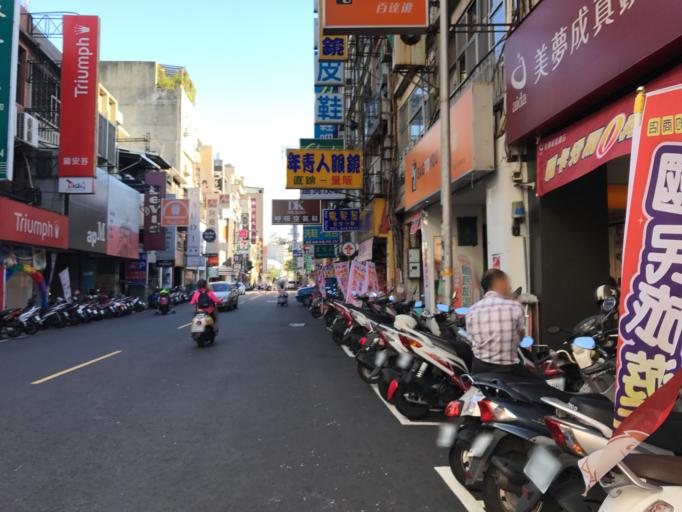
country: TW
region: Taiwan
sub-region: Hsinchu
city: Hsinchu
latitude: 24.8039
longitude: 120.9683
